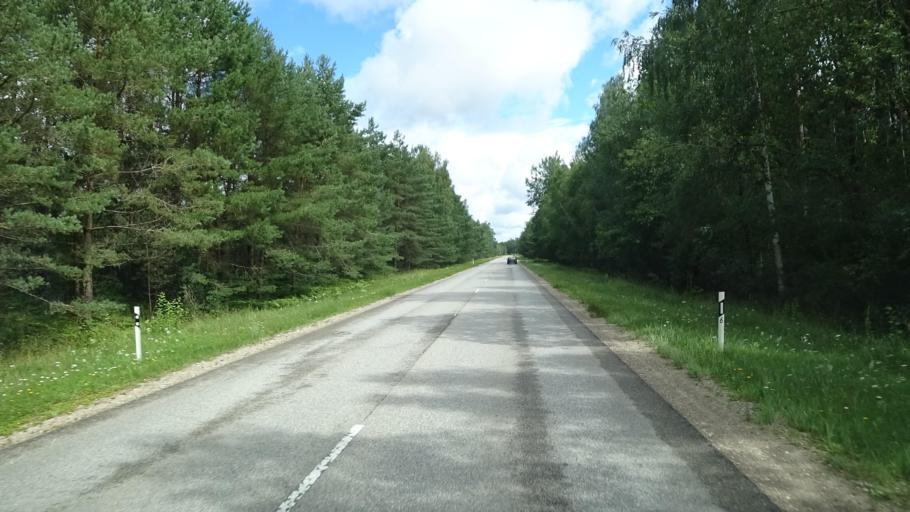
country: LV
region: Grobina
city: Grobina
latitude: 56.6872
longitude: 21.1518
